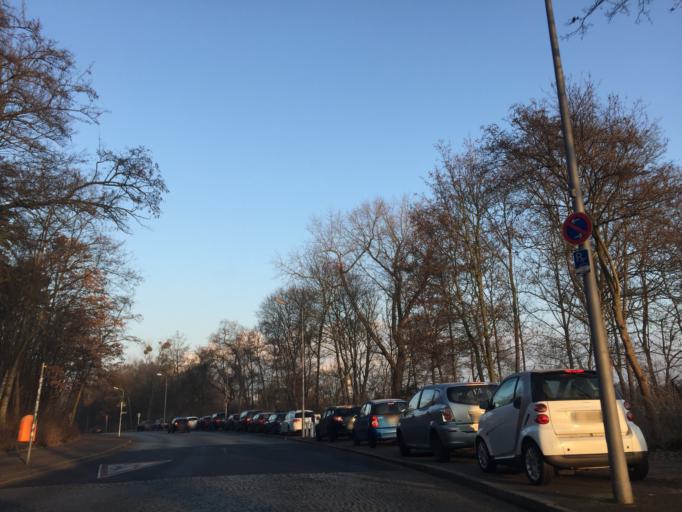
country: DE
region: Berlin
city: Siemensstadt
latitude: 52.5178
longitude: 13.2487
